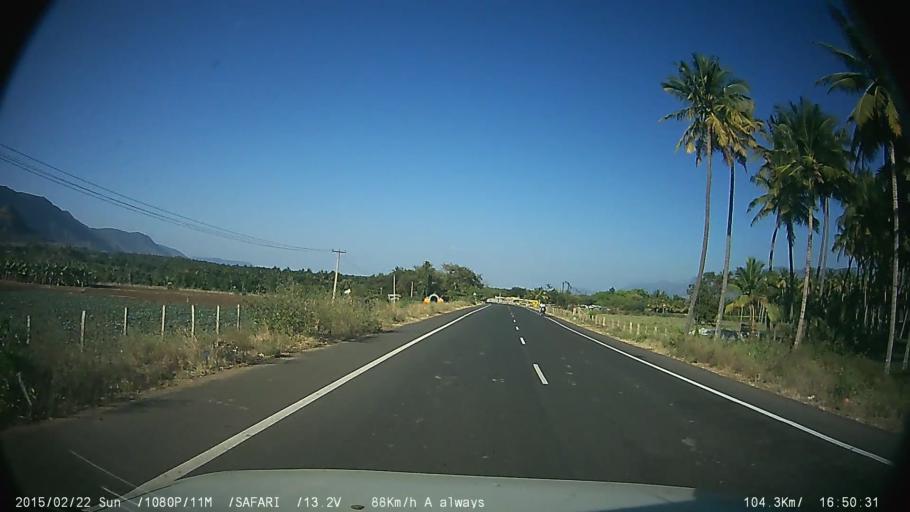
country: IN
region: Tamil Nadu
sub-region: Theni
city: Gudalur
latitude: 9.6424
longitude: 77.2108
